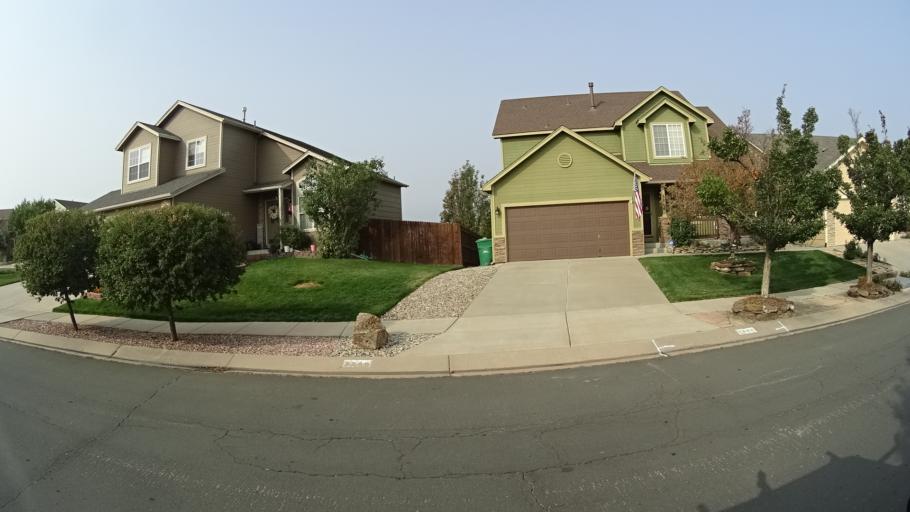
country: US
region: Colorado
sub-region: El Paso County
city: Cimarron Hills
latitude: 38.9347
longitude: -104.7373
